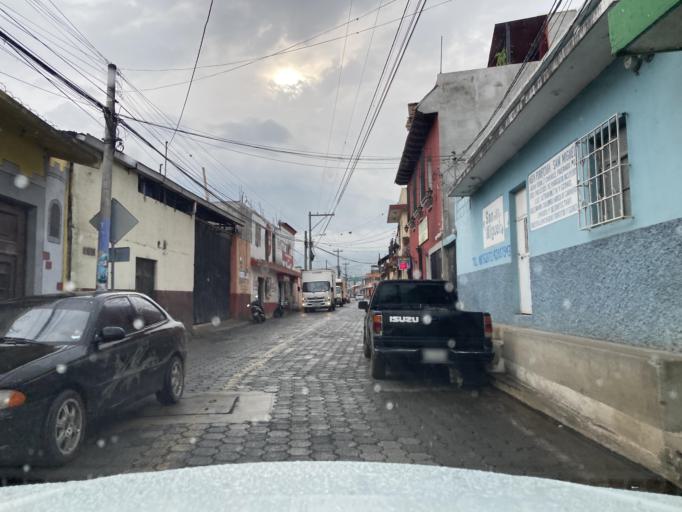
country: GT
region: Sacatepequez
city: San Miguel Duenas
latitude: 14.5246
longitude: -90.7987
